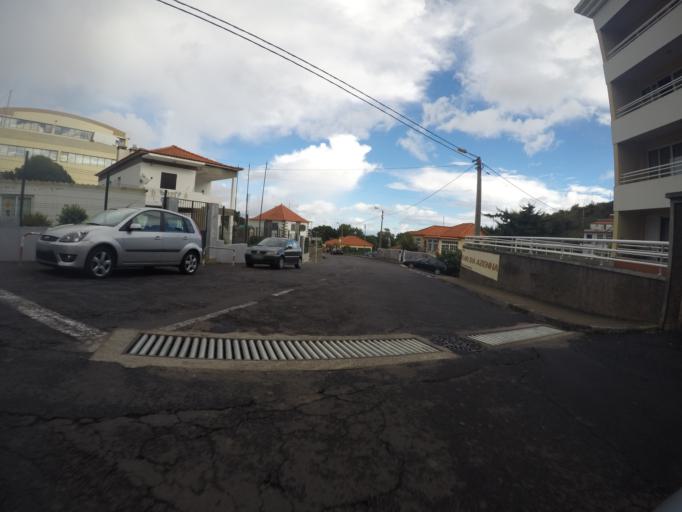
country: PT
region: Madeira
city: Canico
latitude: 32.6527
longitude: -16.8449
